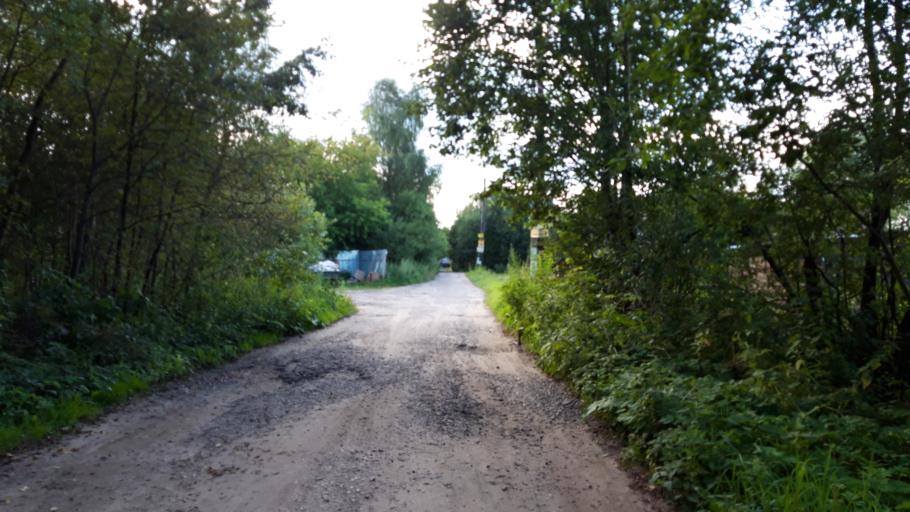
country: RU
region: Tverskaya
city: Konakovo
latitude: 56.6724
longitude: 36.7298
